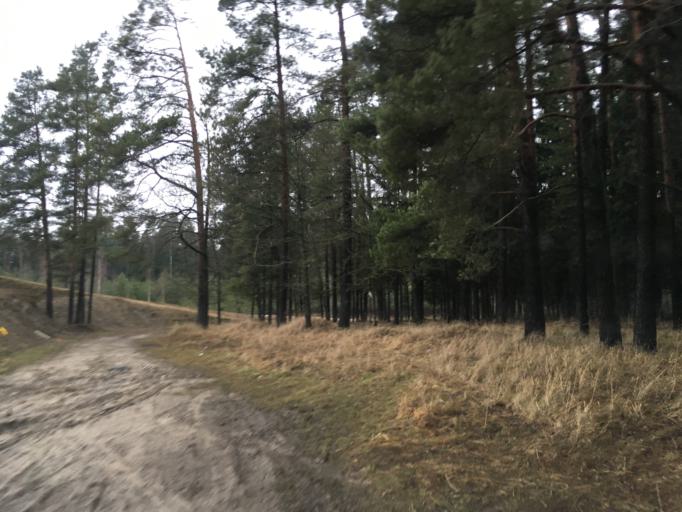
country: LV
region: Ozolnieku
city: Ozolnieki
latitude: 56.6934
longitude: 23.7835
